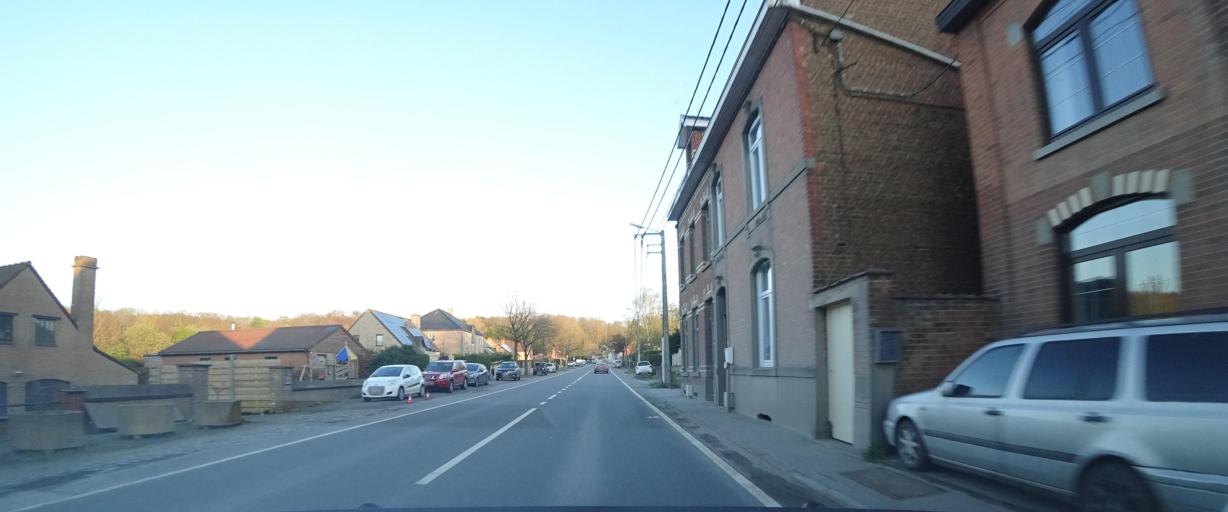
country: BE
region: Wallonia
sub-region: Province du Brabant Wallon
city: Tubize
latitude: 50.6411
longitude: 4.1932
